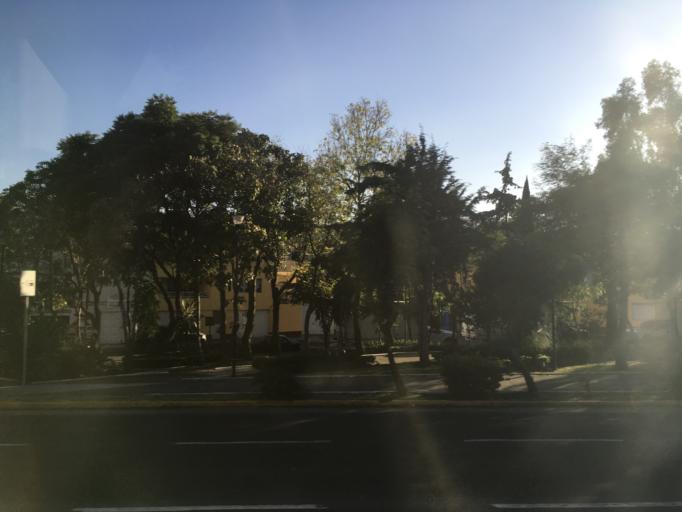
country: MX
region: Mexico City
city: Polanco
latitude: 19.3962
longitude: -99.2072
